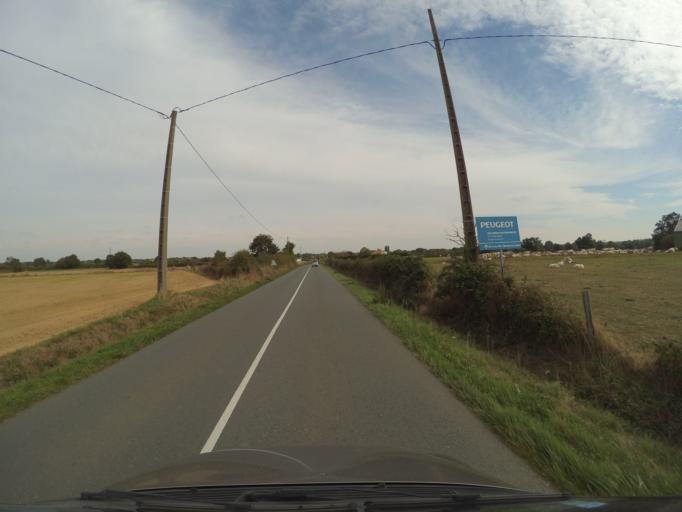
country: FR
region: Pays de la Loire
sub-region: Departement de Maine-et-Loire
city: Melay
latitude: 47.2139
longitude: -0.6224
